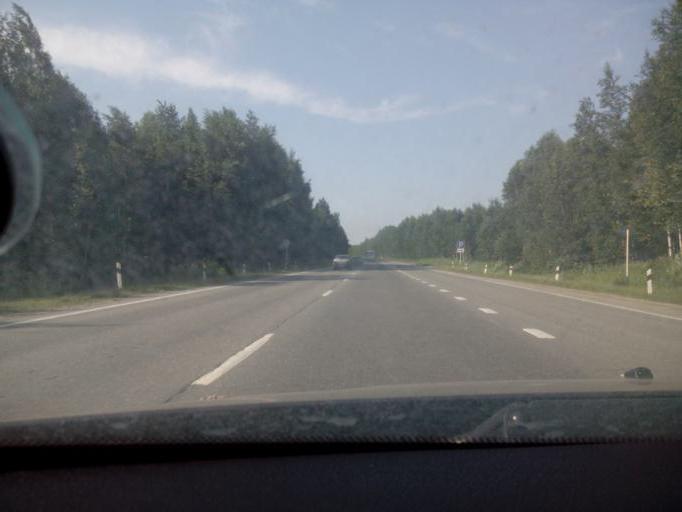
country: RU
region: Sverdlovsk
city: Verkh-Neyvinskiy
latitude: 57.2774
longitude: 60.2962
